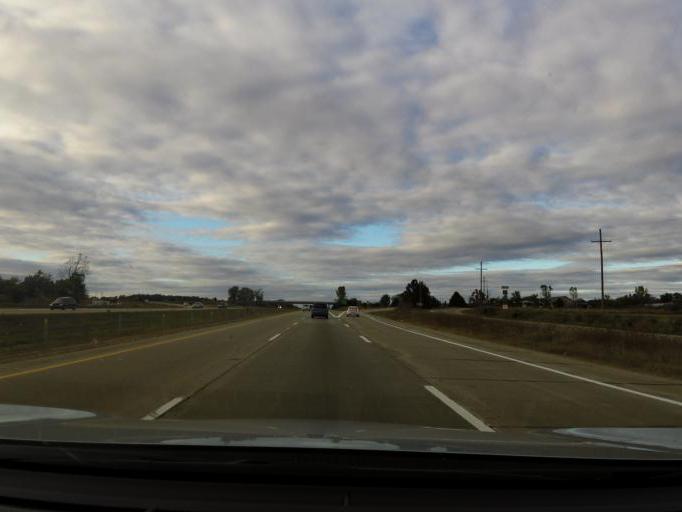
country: US
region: Michigan
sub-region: Genesee County
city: Fenton
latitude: 42.6728
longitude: -83.7594
